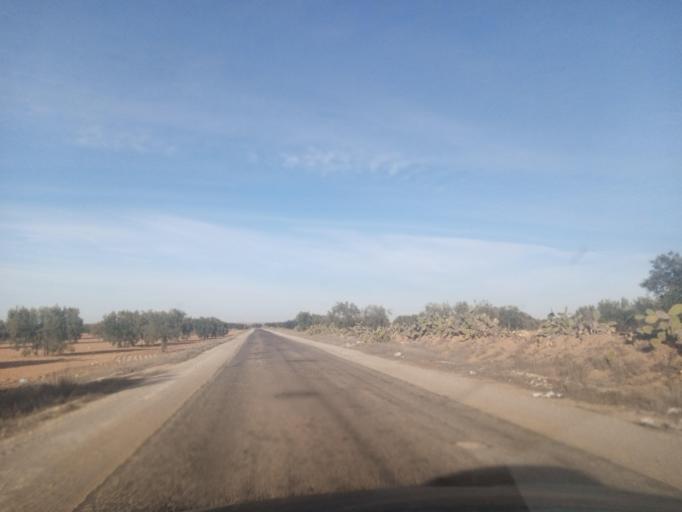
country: TN
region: Safaqis
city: Bi'r `Ali Bin Khalifah
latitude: 34.8842
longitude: 10.1740
